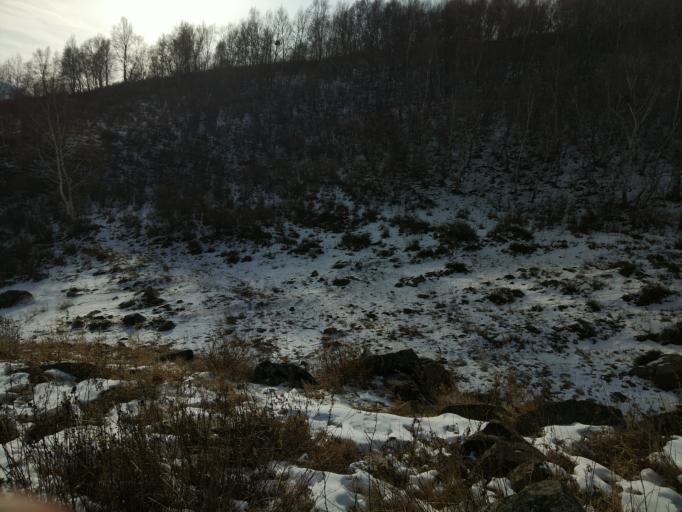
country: CN
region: Hebei
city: Xiwanzi
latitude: 40.8563
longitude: 115.4557
